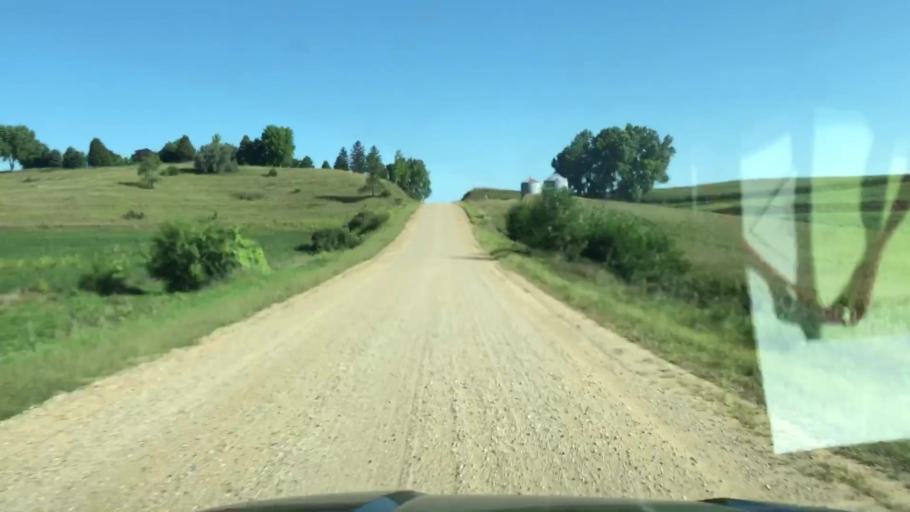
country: US
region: Iowa
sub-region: Woodbury County
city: Sergeant Bluff
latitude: 42.4673
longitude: -96.2921
